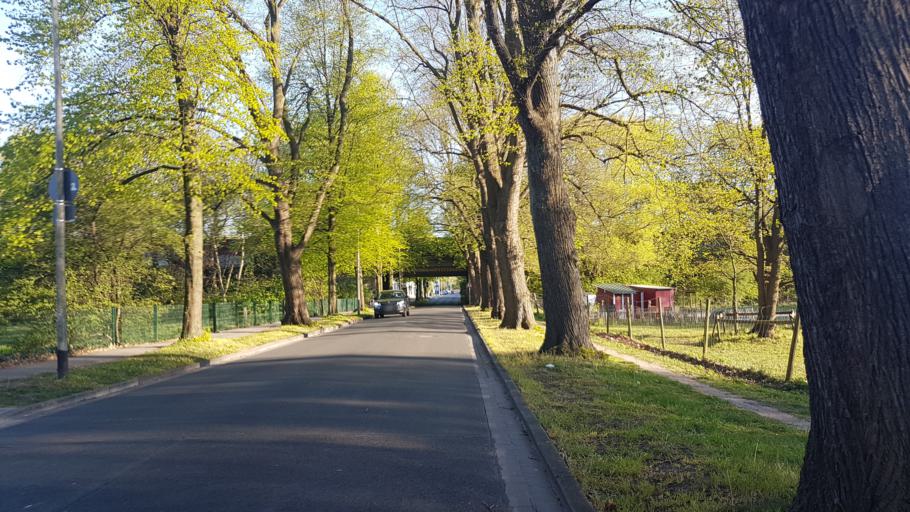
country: DE
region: Lower Saxony
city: Hannover
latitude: 52.3980
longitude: 9.8025
